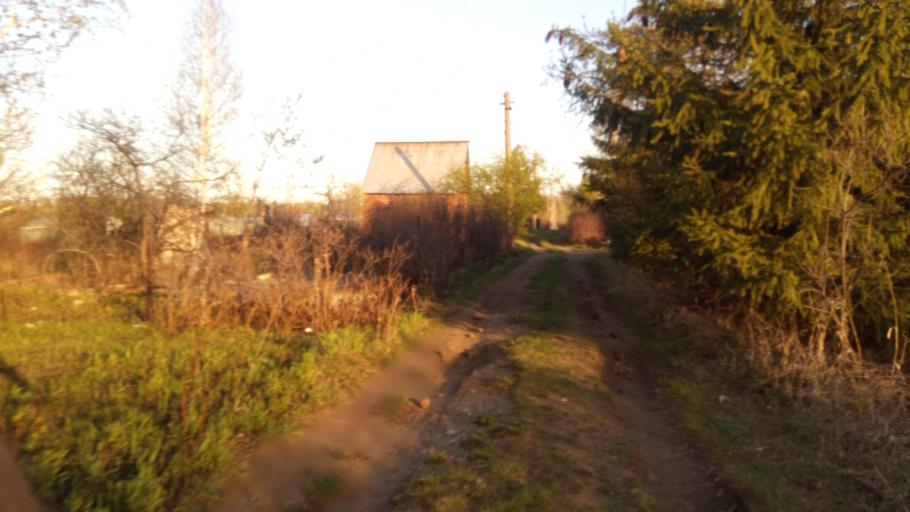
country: RU
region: Chelyabinsk
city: Timiryazevskiy
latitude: 54.9906
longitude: 60.8465
